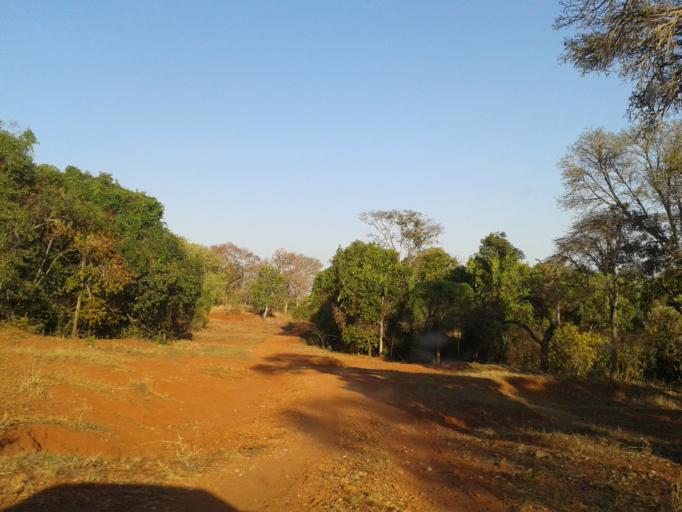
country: BR
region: Minas Gerais
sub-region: Campina Verde
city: Campina Verde
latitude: -19.2636
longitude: -49.6111
